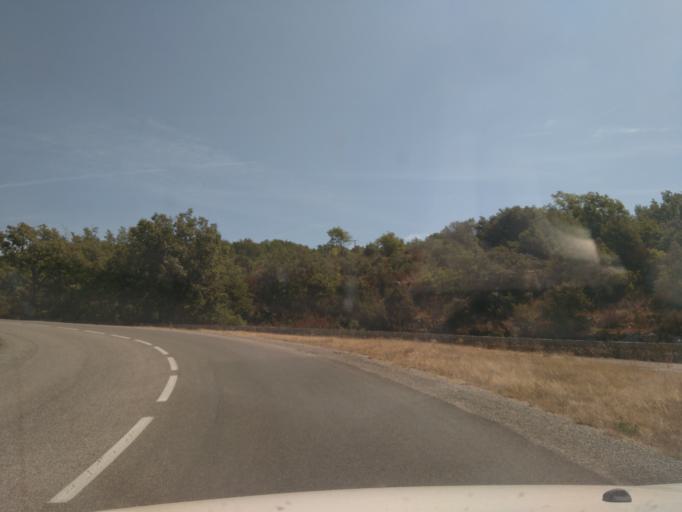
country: FR
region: Provence-Alpes-Cote d'Azur
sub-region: Departement du Var
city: Regusse
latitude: 43.7100
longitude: 6.0446
